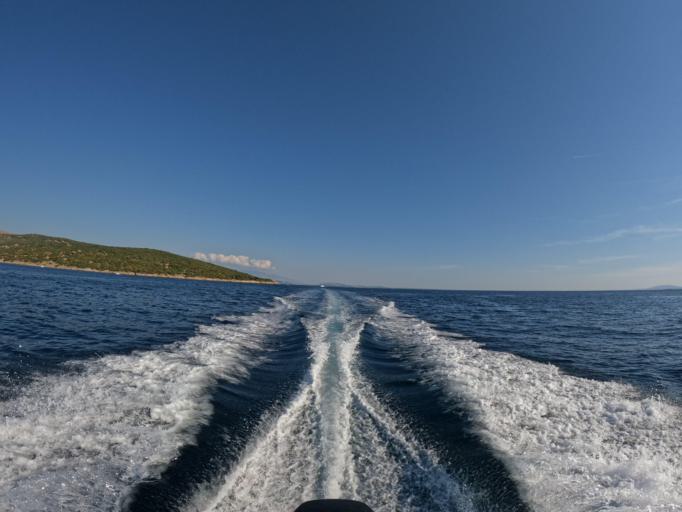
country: HR
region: Primorsko-Goranska
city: Punat
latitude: 44.9863
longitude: 14.6089
